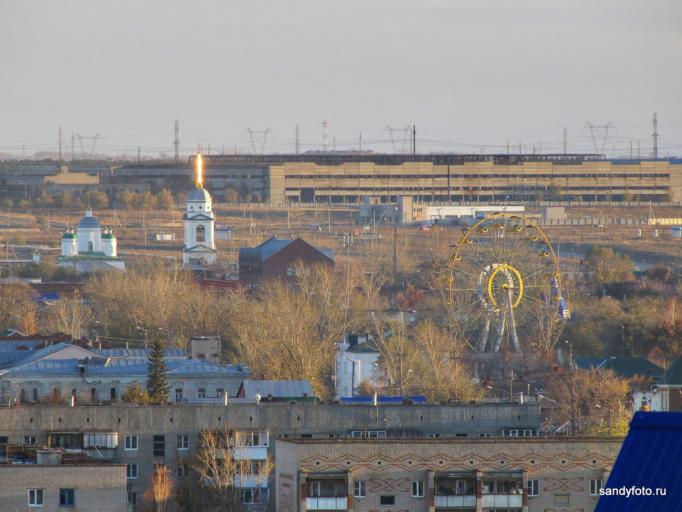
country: RU
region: Chelyabinsk
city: Troitsk
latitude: 54.1005
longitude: 61.5445
